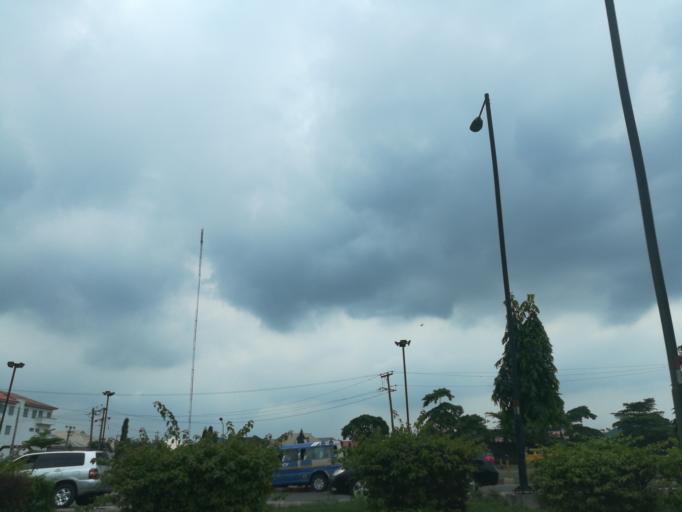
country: NG
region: Lagos
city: Ojota
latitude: 6.6020
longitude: 3.3764
